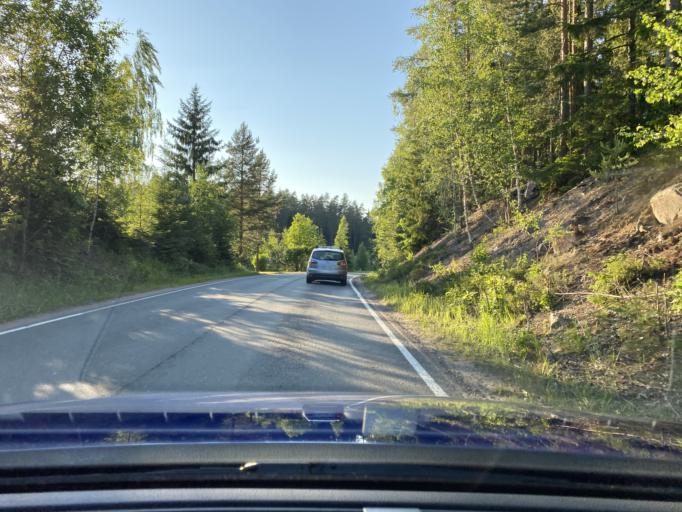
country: FI
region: Haeme
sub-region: Riihimaeki
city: Riihimaeki
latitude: 60.7214
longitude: 24.7049
